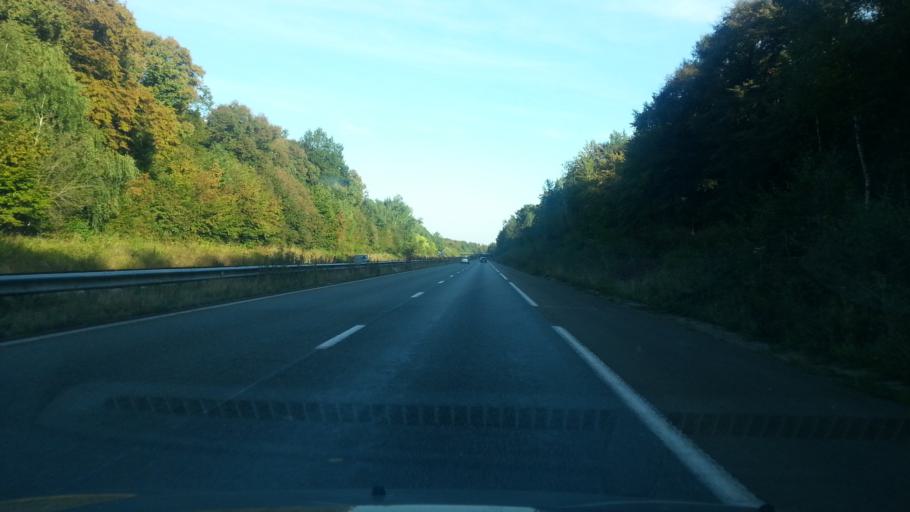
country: FR
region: Picardie
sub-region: Departement de l'Oise
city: Agnetz
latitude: 49.4081
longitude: 2.3493
